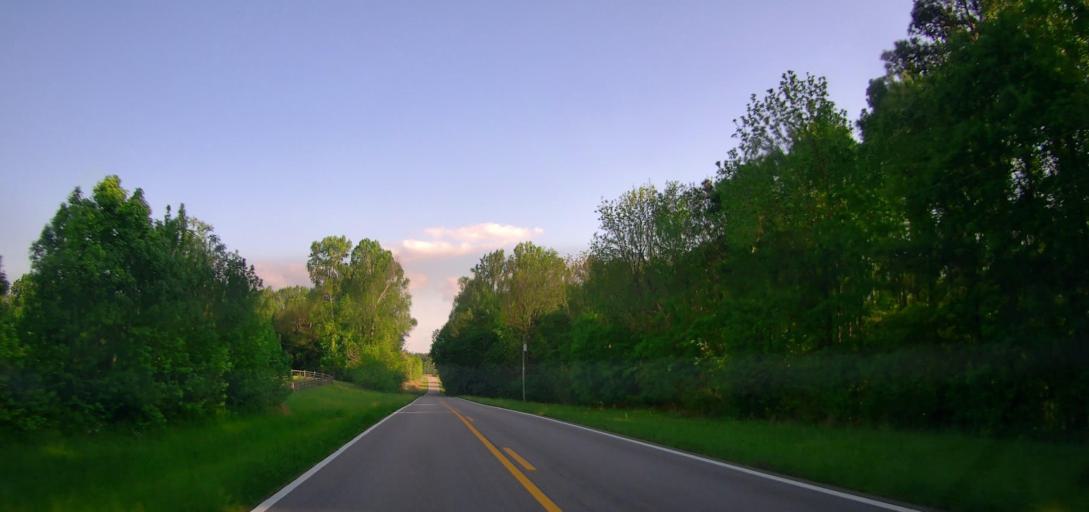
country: US
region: Georgia
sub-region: Putnam County
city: Eatonton
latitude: 33.2953
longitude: -83.3336
